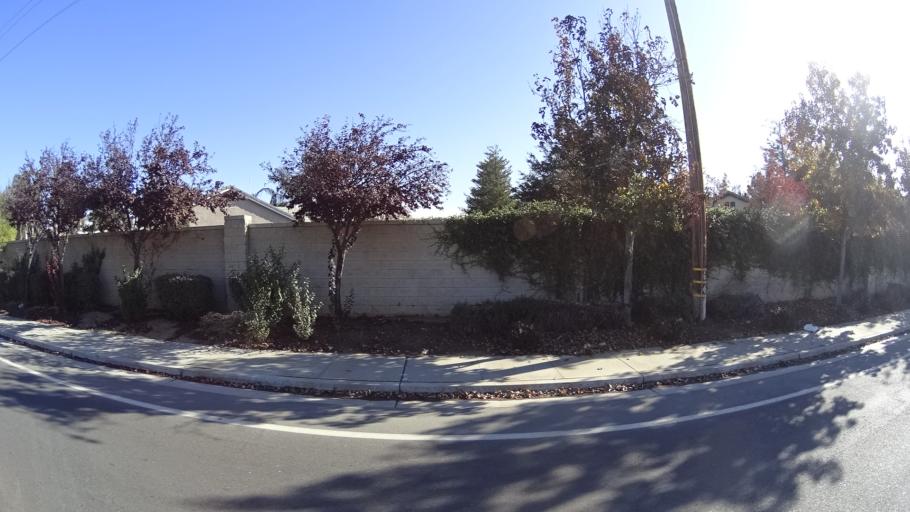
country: US
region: California
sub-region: Kern County
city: Rosedale
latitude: 35.4173
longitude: -119.1455
